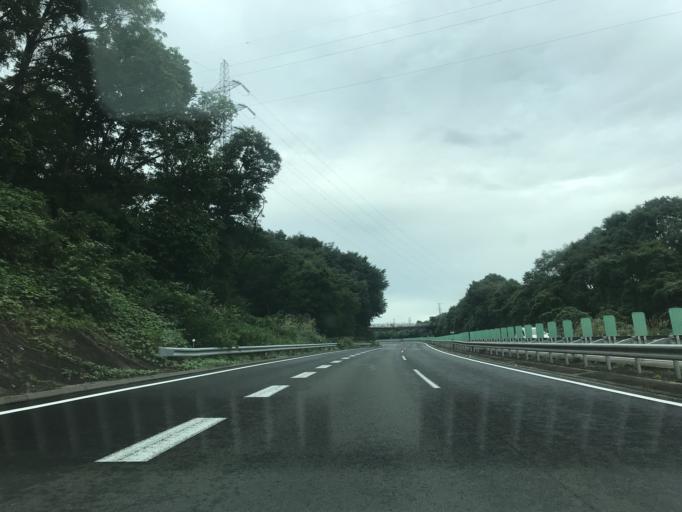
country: JP
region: Miyagi
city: Sendai
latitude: 38.2775
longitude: 140.8097
